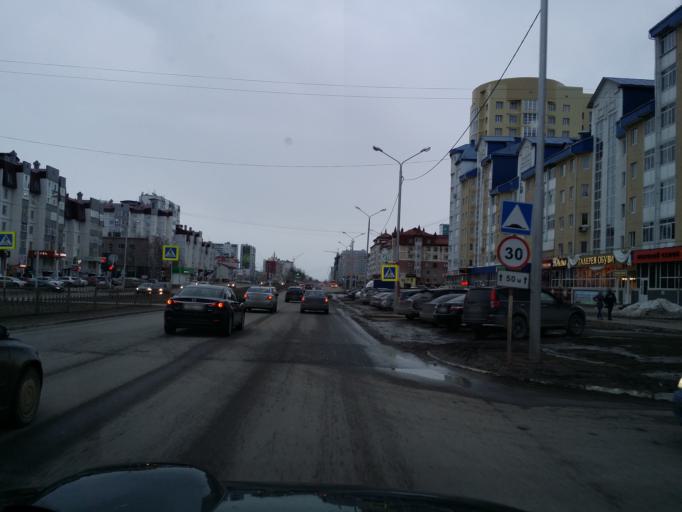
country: RU
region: Khanty-Mansiyskiy Avtonomnyy Okrug
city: Nizhnevartovsk
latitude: 60.9378
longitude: 76.5774
